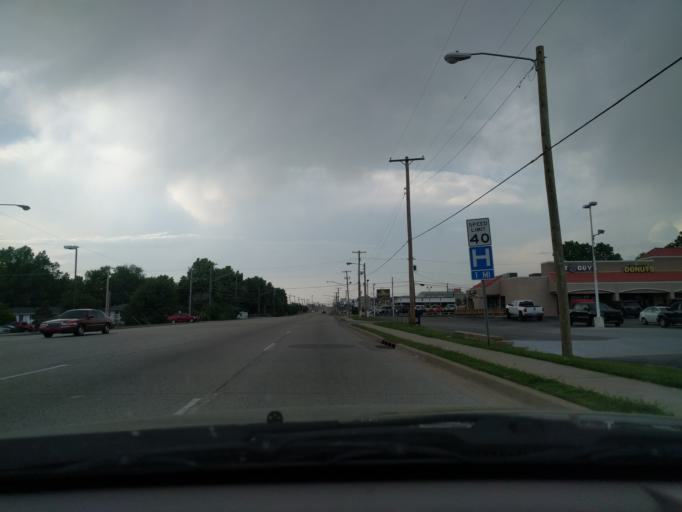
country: US
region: Oklahoma
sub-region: Tulsa County
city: Broken Arrow
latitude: 36.0618
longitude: -95.7974
